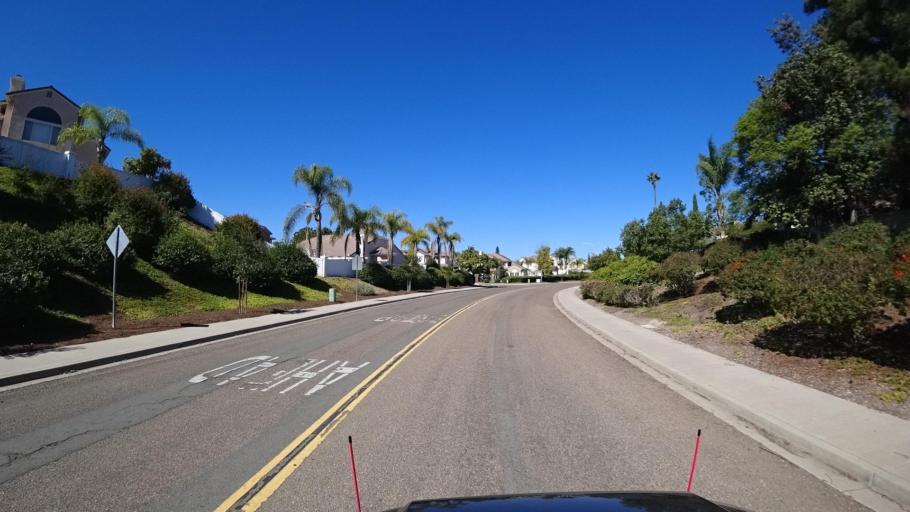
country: US
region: California
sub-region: San Diego County
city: Bonita
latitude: 32.6548
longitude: -116.9862
